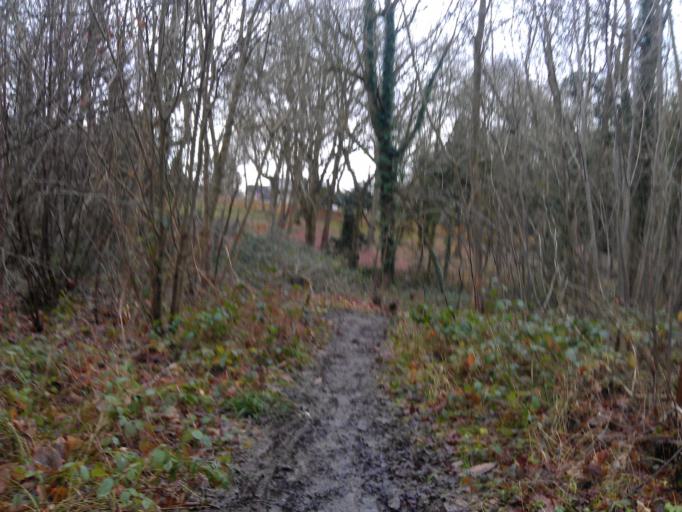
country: GB
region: England
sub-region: Essex
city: Wivenhoe
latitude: 51.8609
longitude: 0.9540
